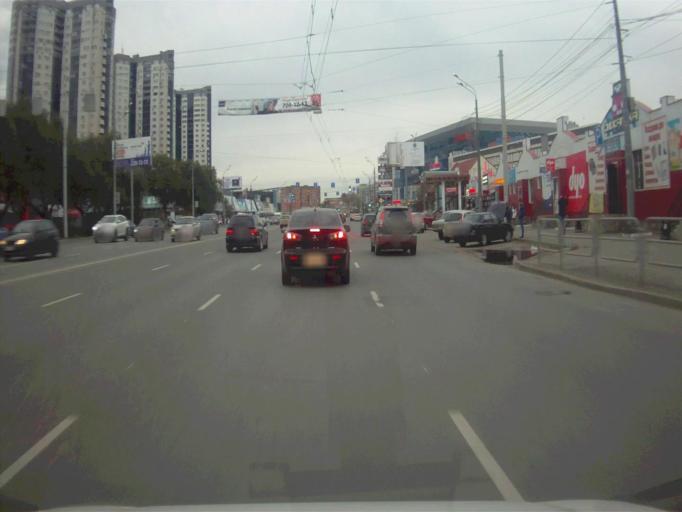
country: RU
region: Chelyabinsk
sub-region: Gorod Chelyabinsk
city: Chelyabinsk
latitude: 55.1702
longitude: 61.3722
